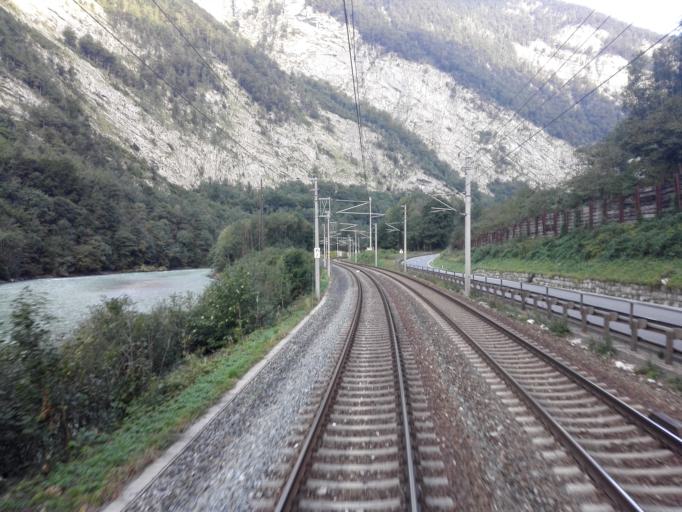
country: AT
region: Salzburg
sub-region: Politischer Bezirk Hallein
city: Golling an der Salzach
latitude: 47.5553
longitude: 13.1677
